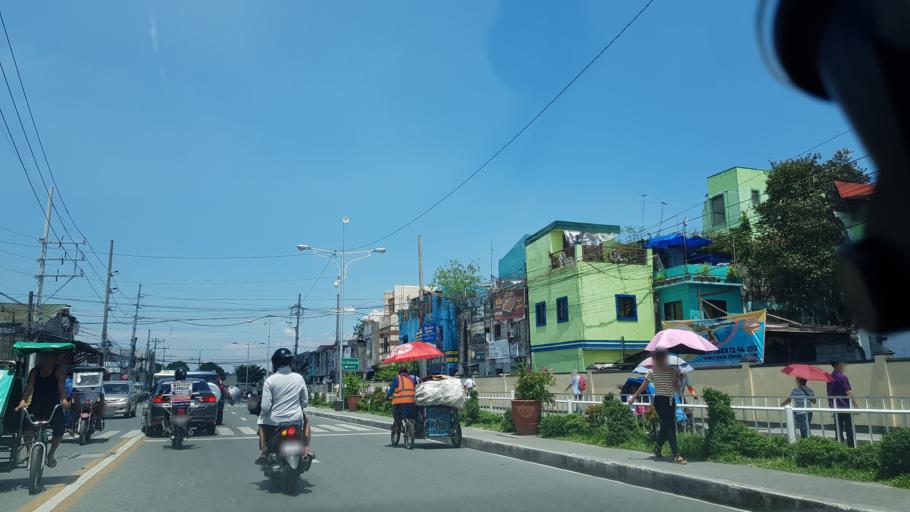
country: PH
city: Sambayanihan People's Village
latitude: 14.4602
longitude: 120.9948
